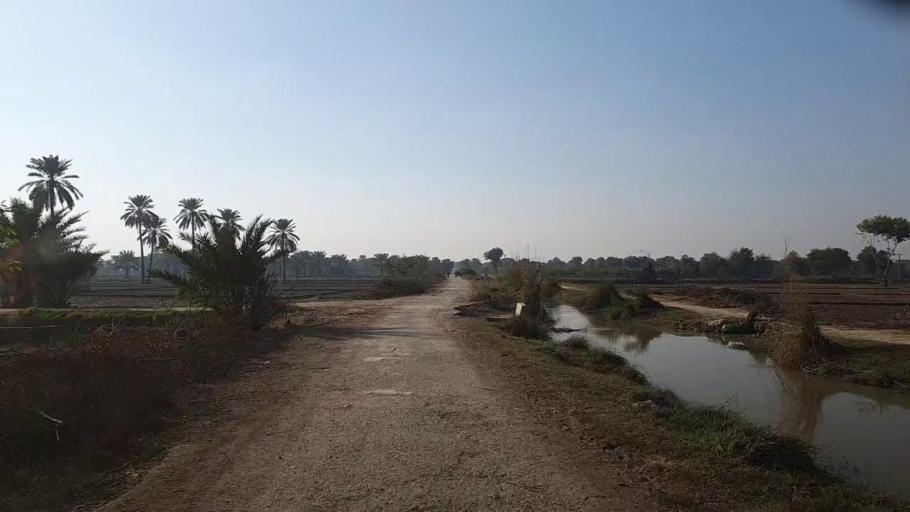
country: PK
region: Sindh
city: Ranipur
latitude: 27.2533
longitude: 68.5375
